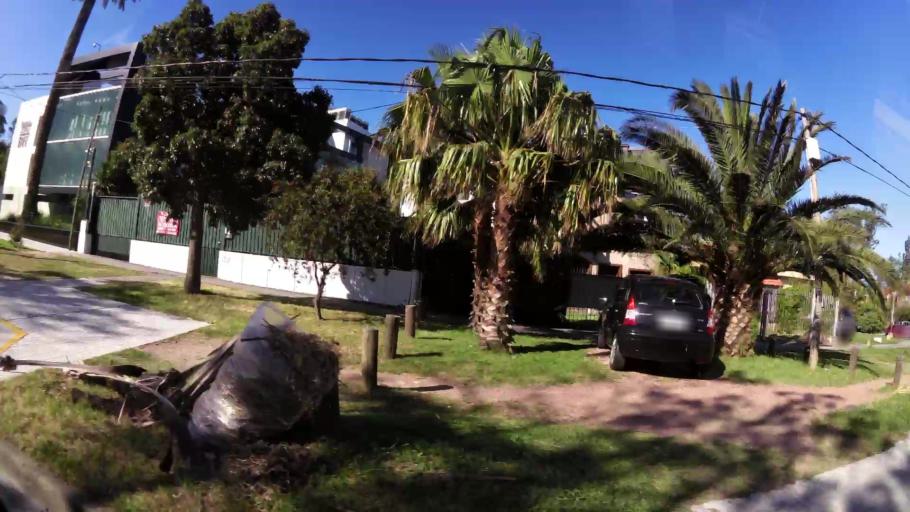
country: UY
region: Canelones
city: Paso de Carrasco
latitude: -34.8872
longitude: -56.0804
